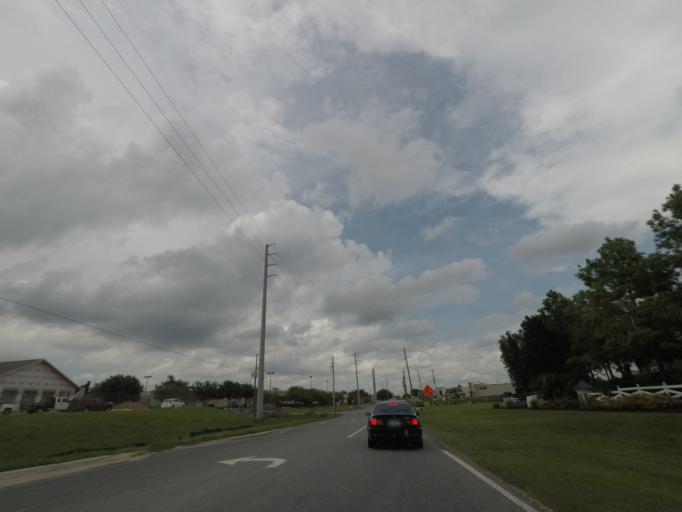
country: US
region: Florida
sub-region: Polk County
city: Loughman
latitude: 28.2565
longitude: -81.5906
